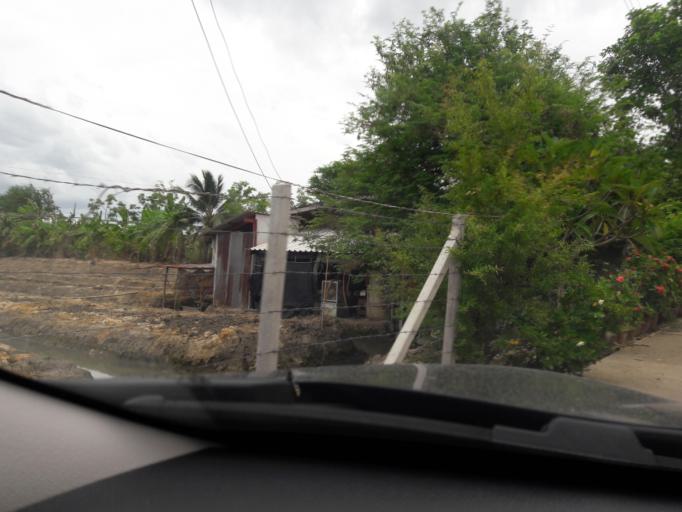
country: TH
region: Ratchaburi
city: Bang Phae
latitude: 13.6309
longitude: 99.9413
